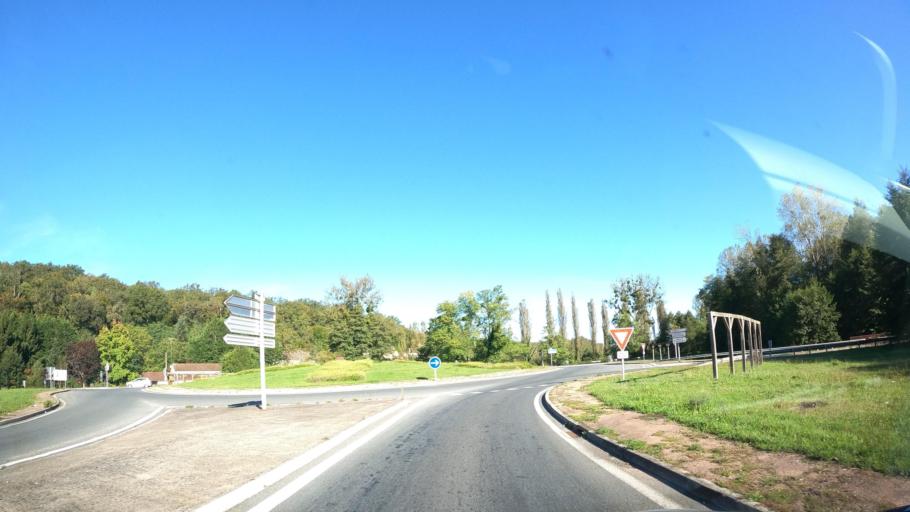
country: FR
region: Aquitaine
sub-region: Departement de la Dordogne
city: Lembras
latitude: 44.8881
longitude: 0.5516
